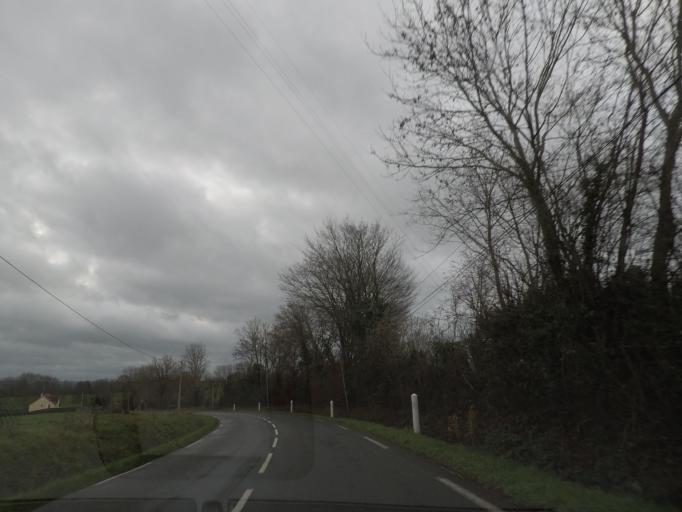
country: FR
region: Pays de la Loire
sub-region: Departement de la Sarthe
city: La Ferte-Bernard
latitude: 48.2051
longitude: 0.6337
